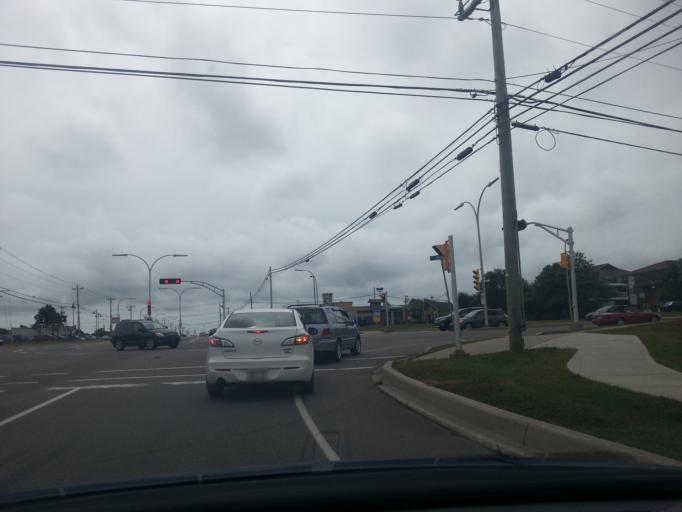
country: CA
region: Prince Edward Island
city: Charlottetown
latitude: 46.2672
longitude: -63.1489
